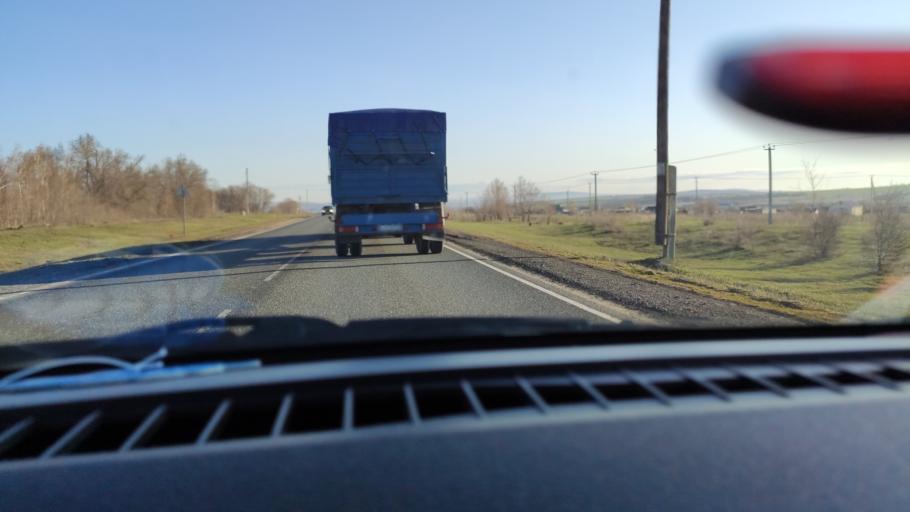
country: RU
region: Saratov
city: Balakovo
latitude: 52.1140
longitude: 47.7503
